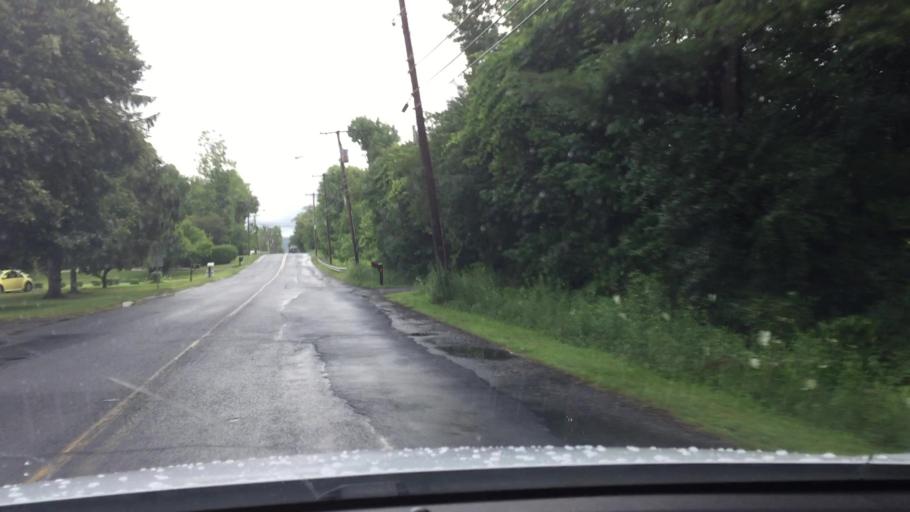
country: US
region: Massachusetts
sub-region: Berkshire County
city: Pittsfield
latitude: 42.4313
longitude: -73.1969
